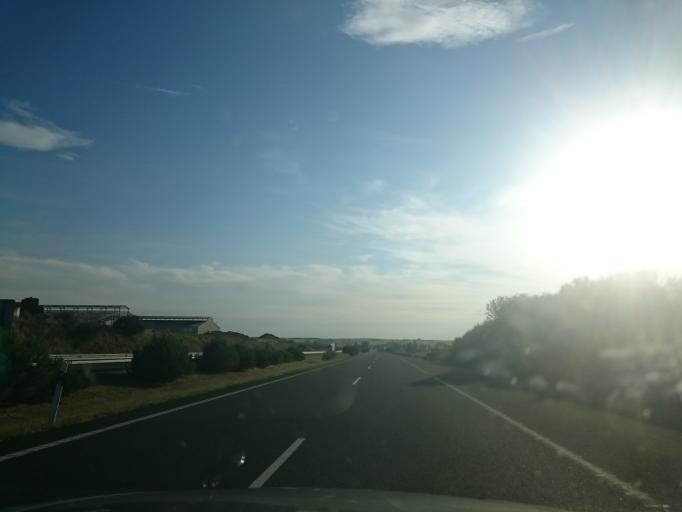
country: ES
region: Castille and Leon
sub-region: Provincia de Palencia
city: Ledigos
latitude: 42.3667
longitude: -4.8853
